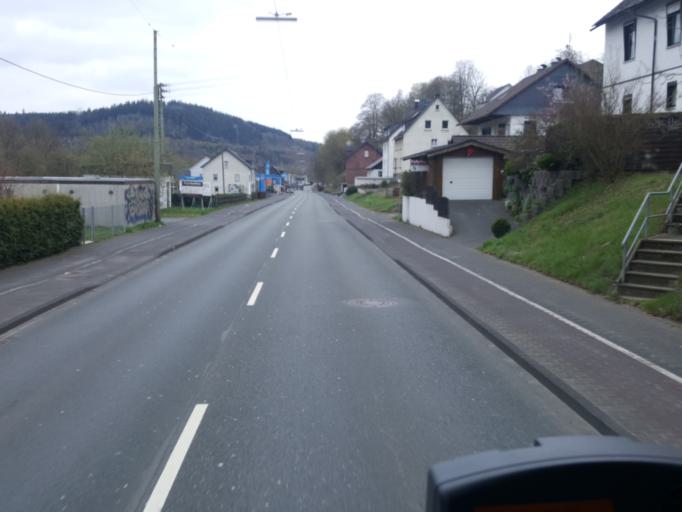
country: DE
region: North Rhine-Westphalia
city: Hilchenbach
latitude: 50.9887
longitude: 8.1032
